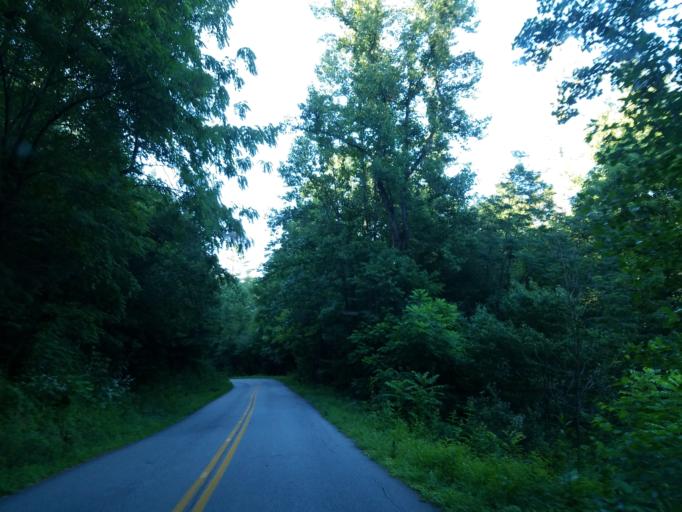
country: US
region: Georgia
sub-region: Union County
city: Blairsville
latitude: 34.7635
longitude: -84.0971
